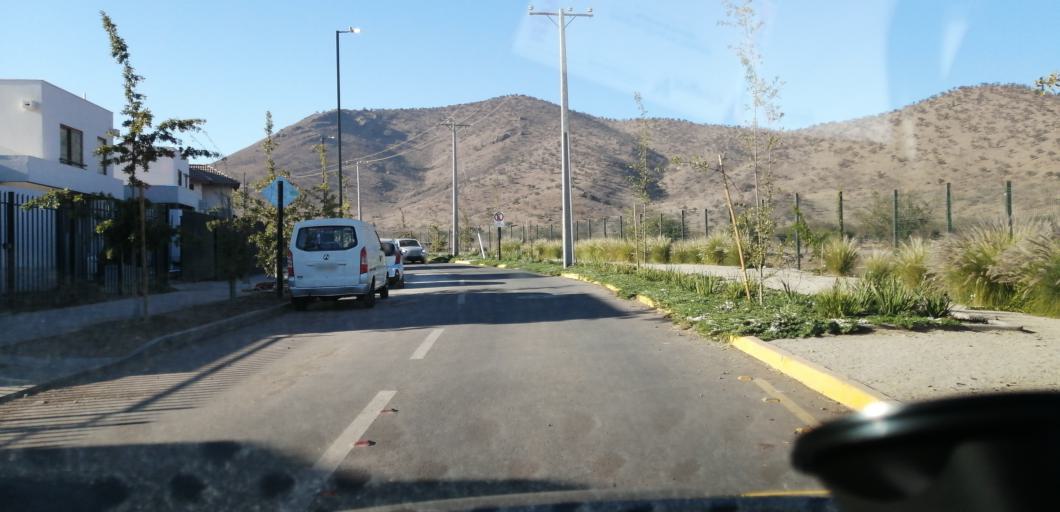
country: CL
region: Santiago Metropolitan
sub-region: Provincia de Talagante
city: Penaflor
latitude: -33.4685
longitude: -70.8625
